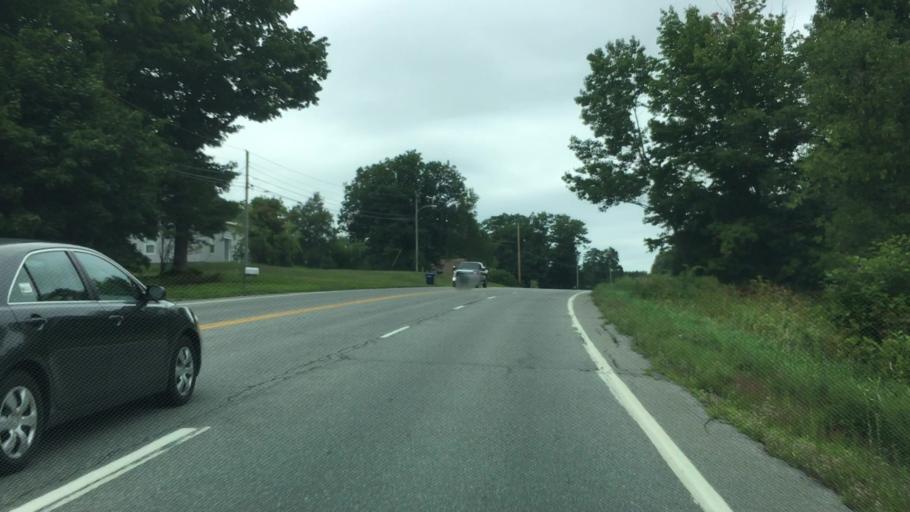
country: US
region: Maine
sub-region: Penobscot County
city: Orrington
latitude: 44.7068
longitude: -68.8465
